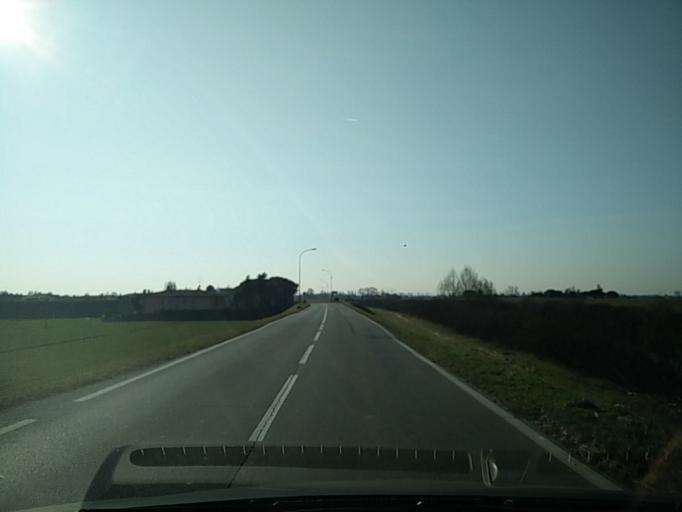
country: IT
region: Veneto
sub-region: Provincia di Venezia
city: Torre di Mosto
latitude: 45.6990
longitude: 12.7086
